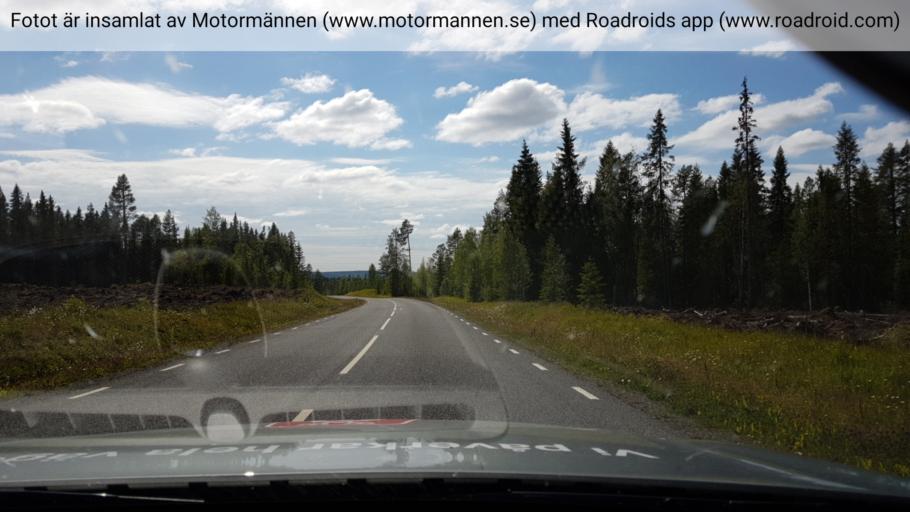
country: SE
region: Jaemtland
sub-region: OEstersunds Kommun
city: Lit
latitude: 63.3212
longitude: 15.0662
